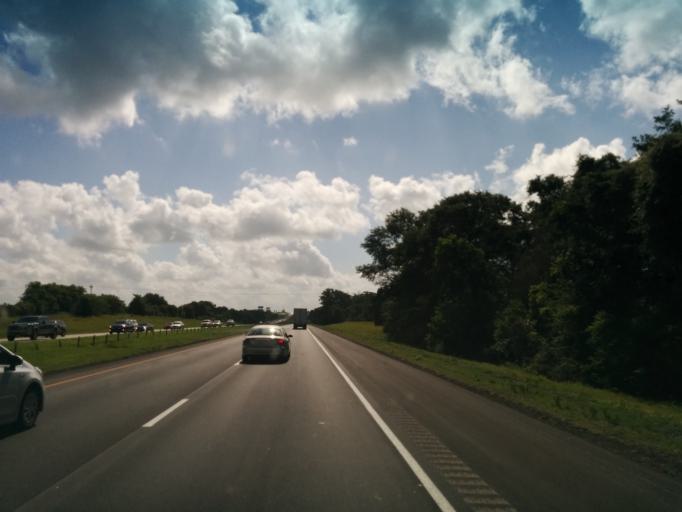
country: US
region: Texas
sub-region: Colorado County
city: Weimar
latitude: 29.6899
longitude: -96.8013
